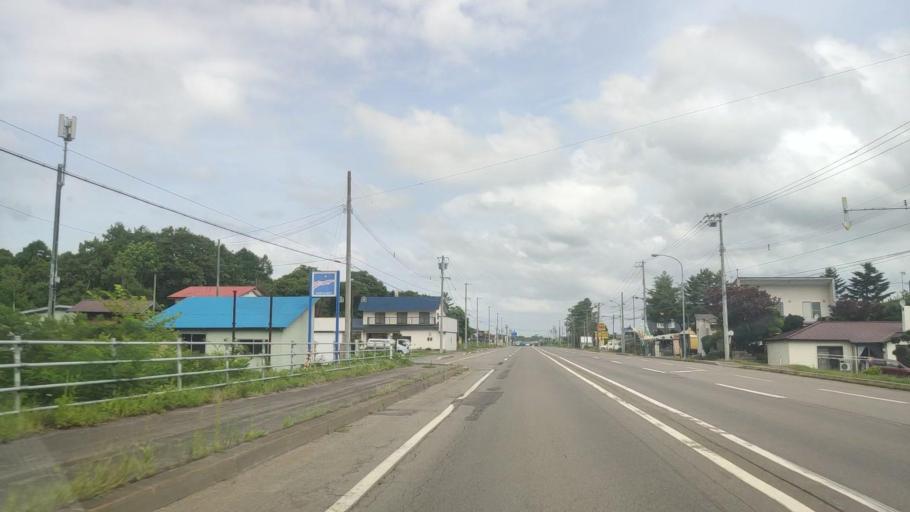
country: JP
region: Hokkaido
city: Nanae
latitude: 42.0013
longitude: 140.6342
